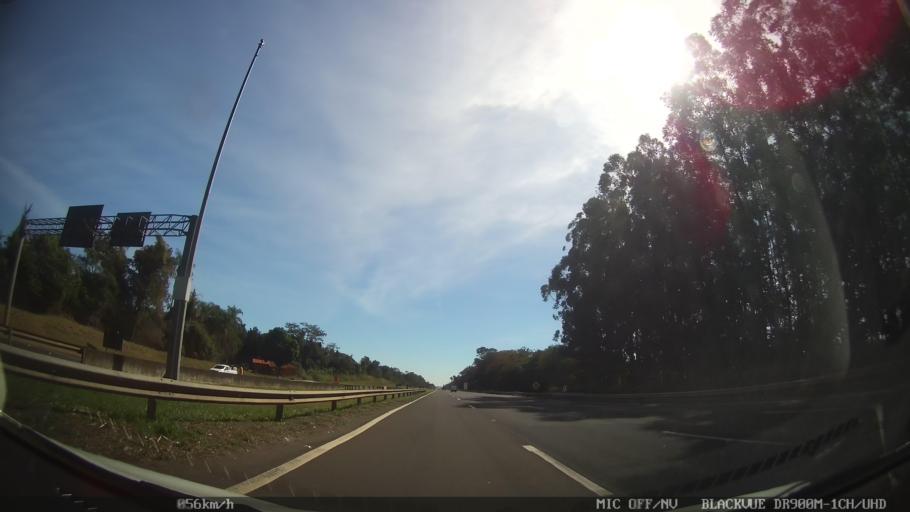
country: BR
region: Sao Paulo
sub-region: Pirassununga
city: Pirassununga
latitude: -21.9553
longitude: -47.4603
